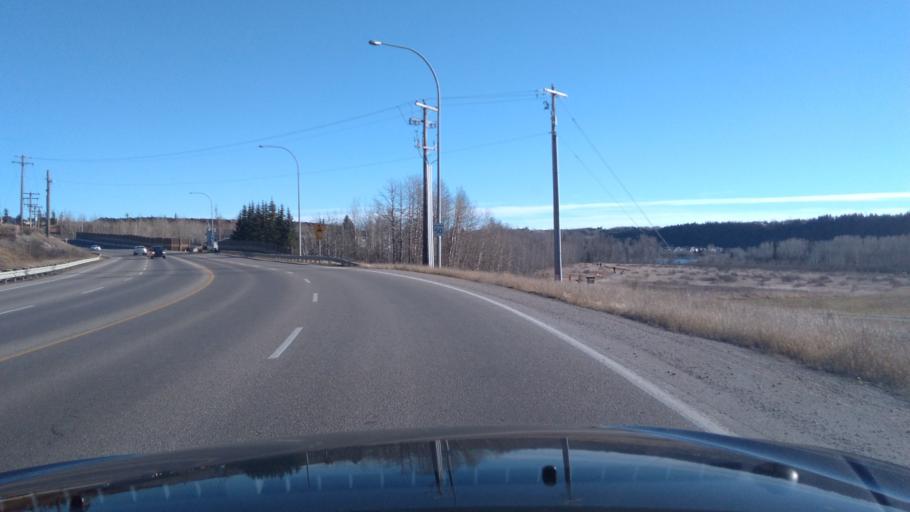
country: CA
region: Alberta
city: Cochrane
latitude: 51.1838
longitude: -114.4843
